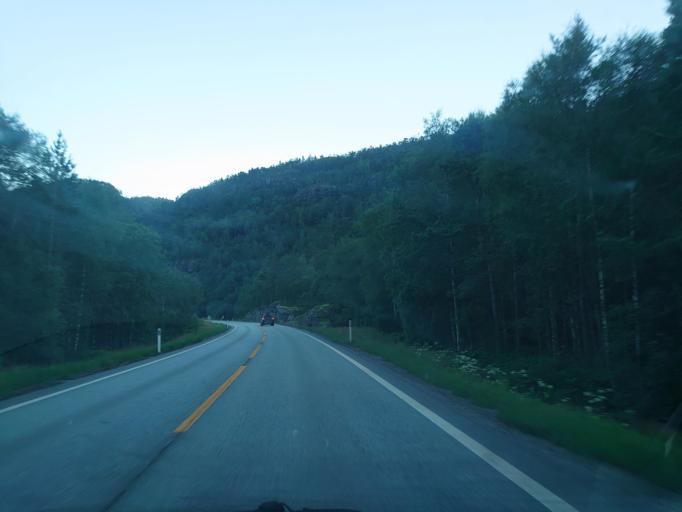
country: NO
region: Hordaland
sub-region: Osteroy
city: Lonevag
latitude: 60.6629
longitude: 5.4835
